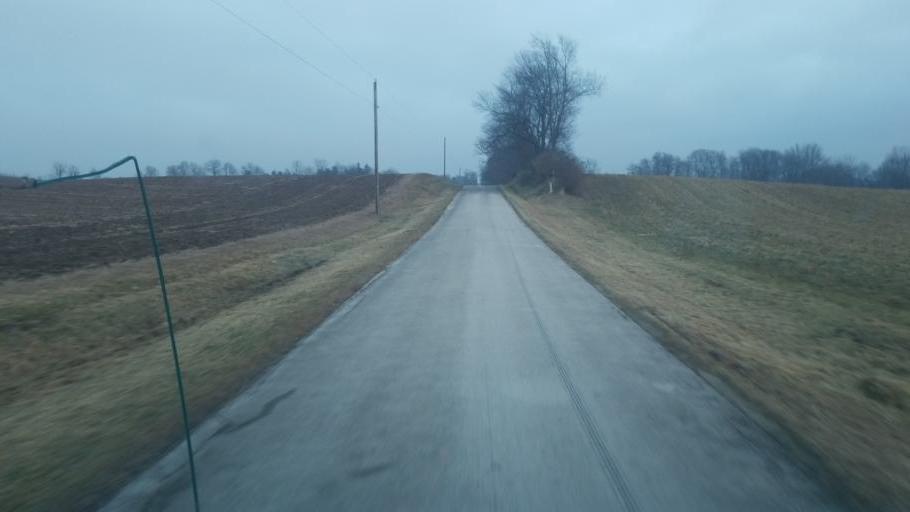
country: US
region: Ohio
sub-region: Seneca County
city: Tiffin
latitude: 41.0074
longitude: -83.2376
